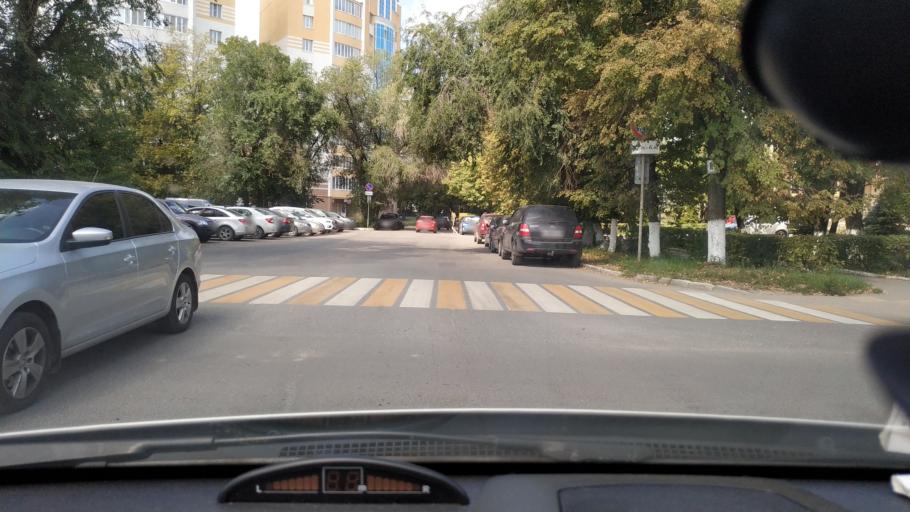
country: RU
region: Rjazan
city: Ryazan'
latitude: 54.6235
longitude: 39.7112
